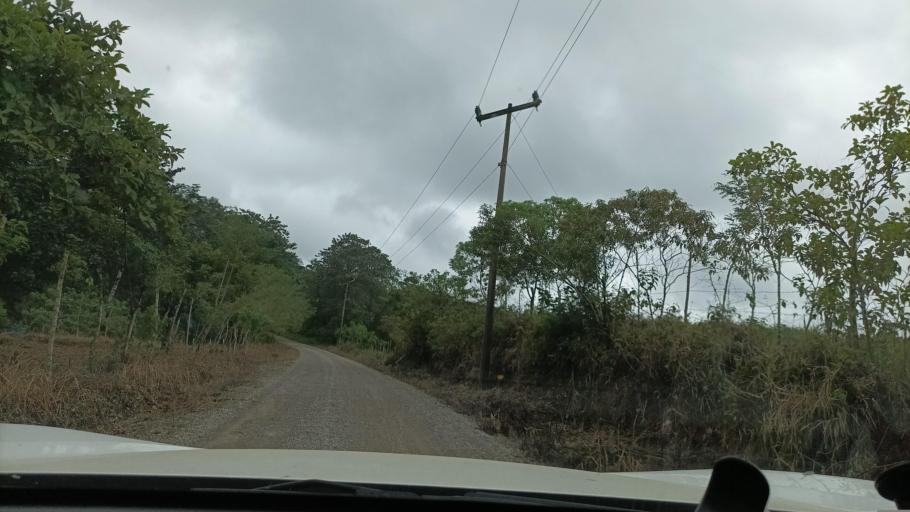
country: MX
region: Veracruz
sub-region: Uxpanapa
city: Poblado 10
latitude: 17.4227
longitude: -94.4183
